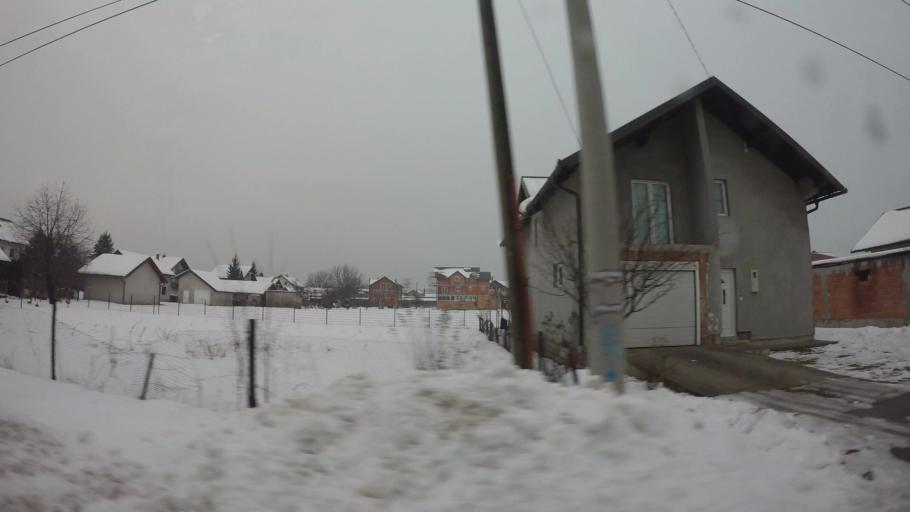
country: BA
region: Federation of Bosnia and Herzegovina
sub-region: Kanton Sarajevo
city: Sarajevo
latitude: 43.8475
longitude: 18.3133
